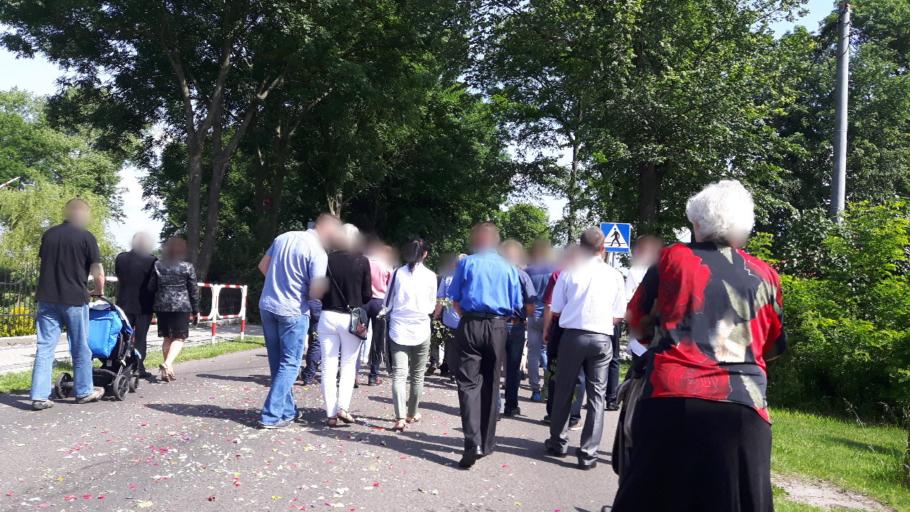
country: PL
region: West Pomeranian Voivodeship
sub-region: Powiat goleniowski
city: Goleniow
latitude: 53.4805
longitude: 14.7748
